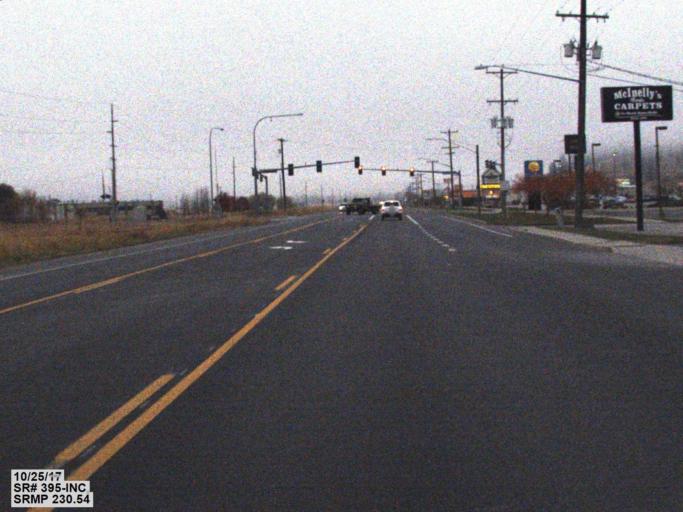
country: US
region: Washington
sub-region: Stevens County
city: Colville
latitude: 48.5542
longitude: -117.9194
